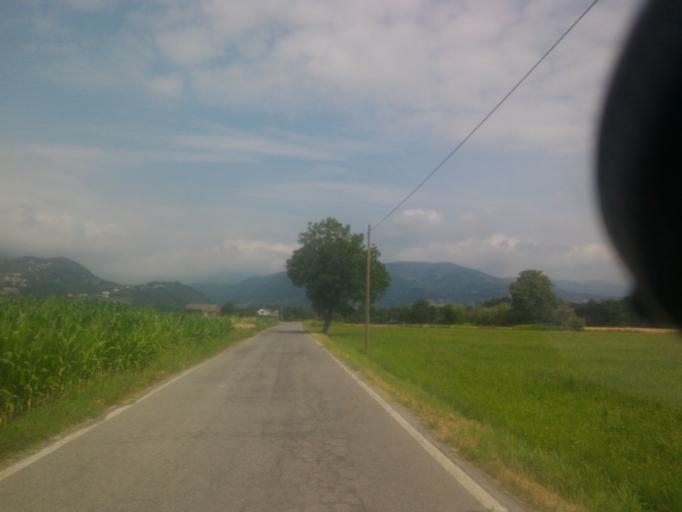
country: IT
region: Piedmont
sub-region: Provincia di Torino
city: Pinerolo
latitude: 44.8663
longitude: 7.3231
